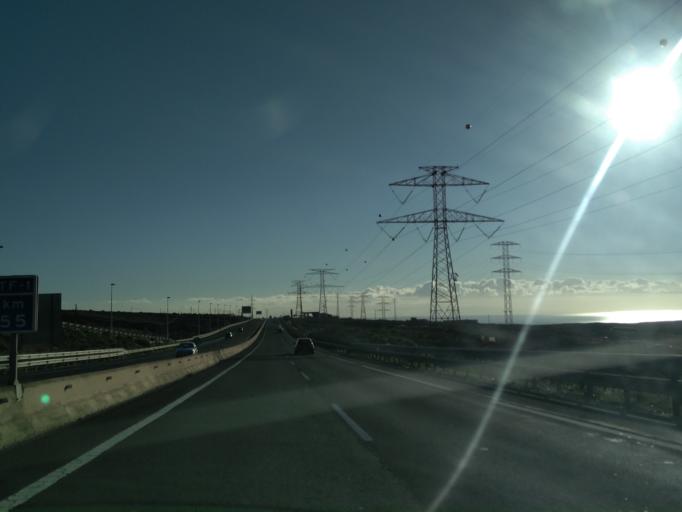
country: ES
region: Canary Islands
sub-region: Provincia de Santa Cruz de Tenerife
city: San Isidro
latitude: 28.0726
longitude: -16.5441
